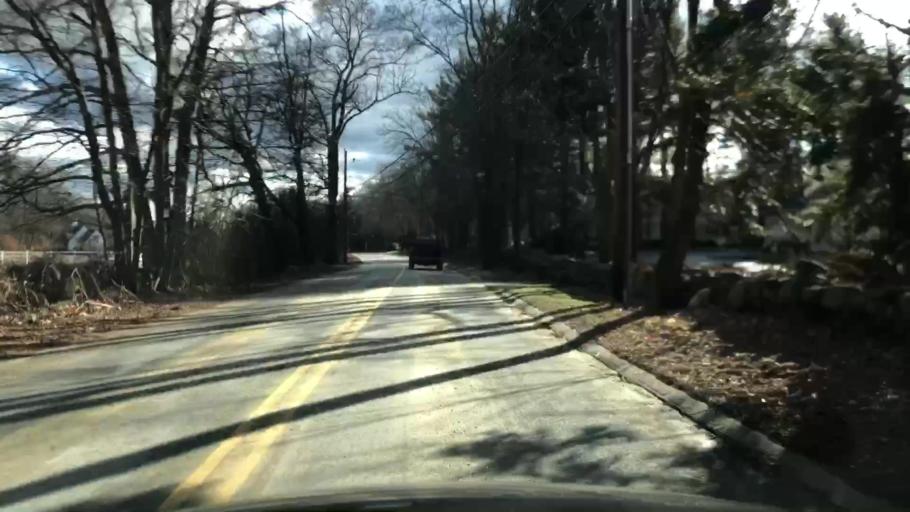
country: US
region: New Hampshire
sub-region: Hillsborough County
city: Mont Vernon
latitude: 42.8897
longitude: -71.6328
